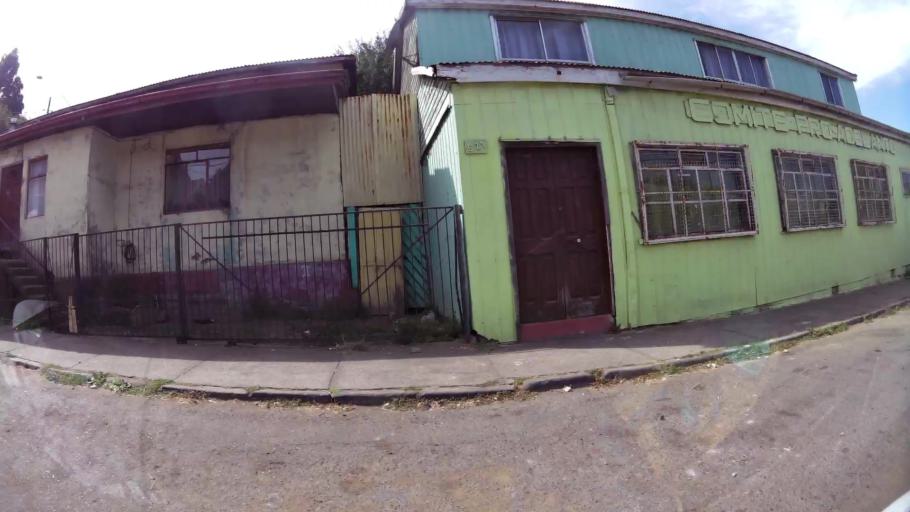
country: CL
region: Biobio
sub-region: Provincia de Concepcion
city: Talcahuano
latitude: -36.7172
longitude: -73.1177
